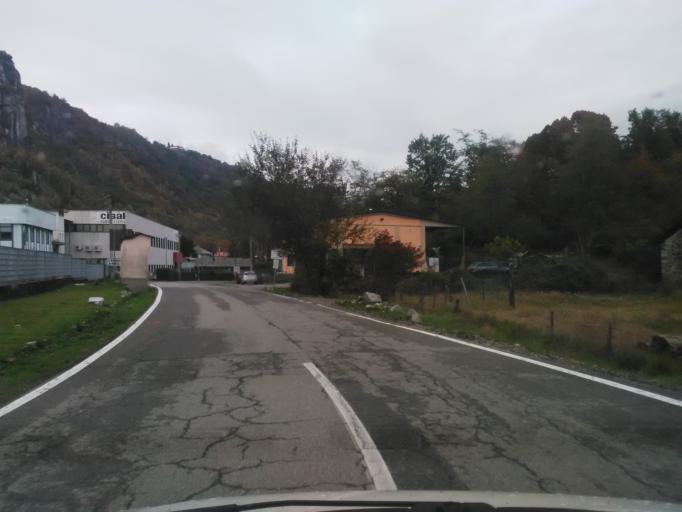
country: IT
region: Piedmont
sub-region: Provincia di Novara
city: Pella
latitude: 45.7842
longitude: 8.3823
